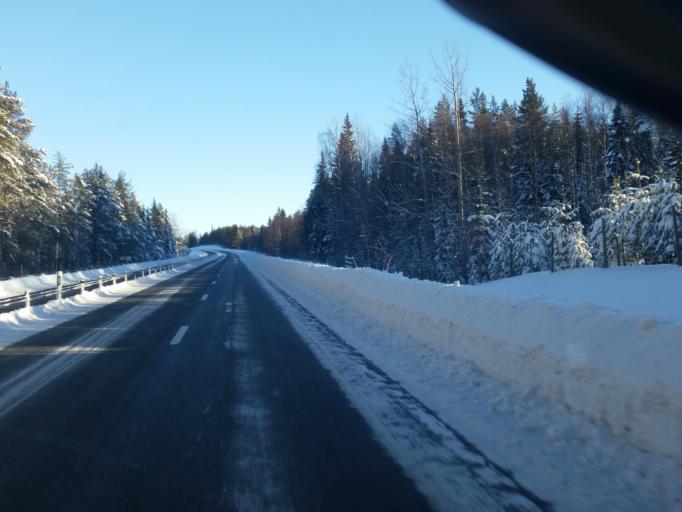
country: SE
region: Norrbotten
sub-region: Pitea Kommun
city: Pitea
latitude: 65.1002
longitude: 21.5052
